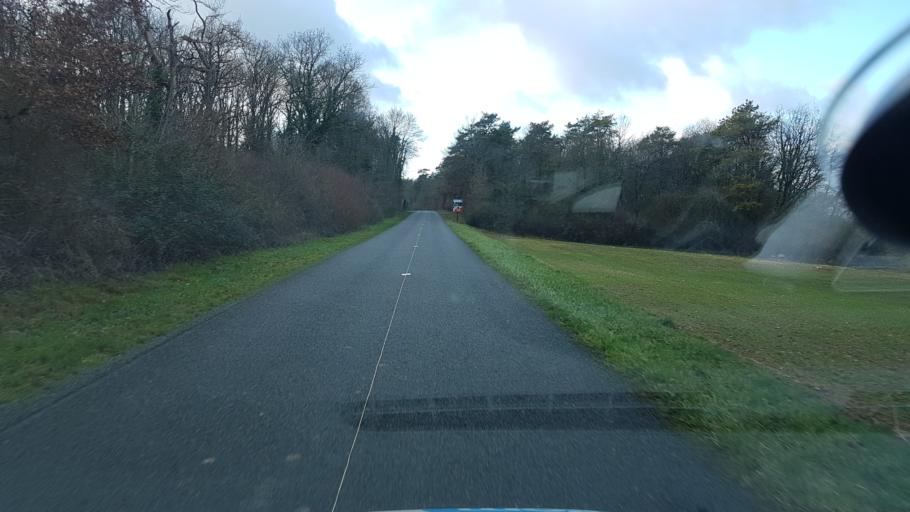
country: FR
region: Ile-de-France
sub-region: Departement de Seine-et-Marne
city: Montigny-sur-Loing
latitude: 48.2758
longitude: 2.7857
